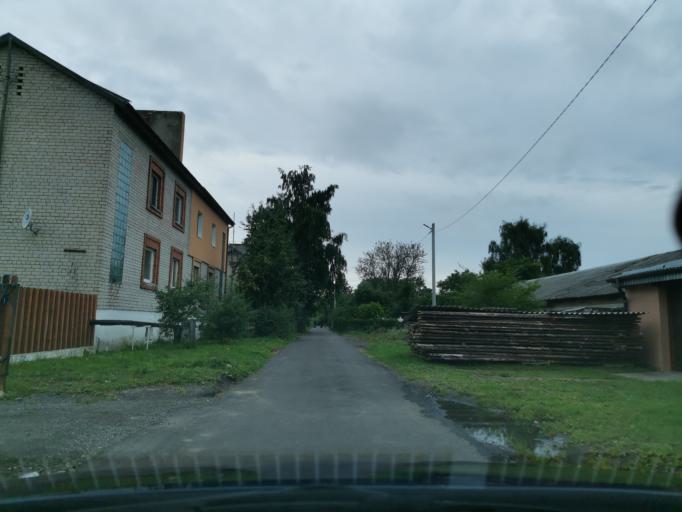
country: LT
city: Nida
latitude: 55.1510
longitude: 20.8528
